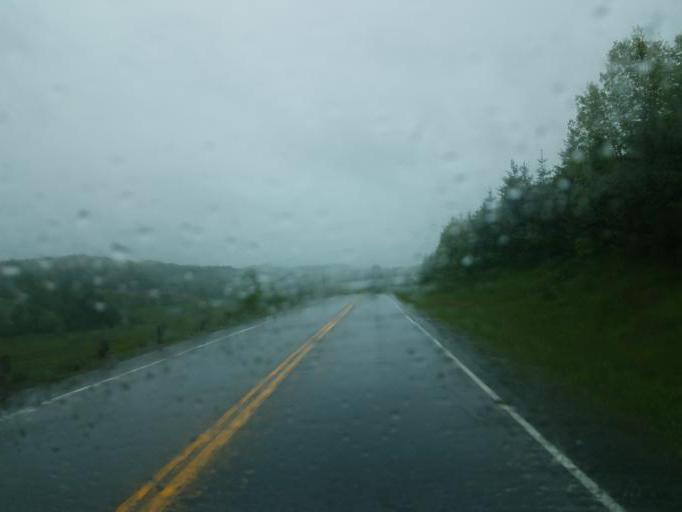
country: US
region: New York
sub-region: Herkimer County
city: Ilion
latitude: 42.9318
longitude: -75.0864
